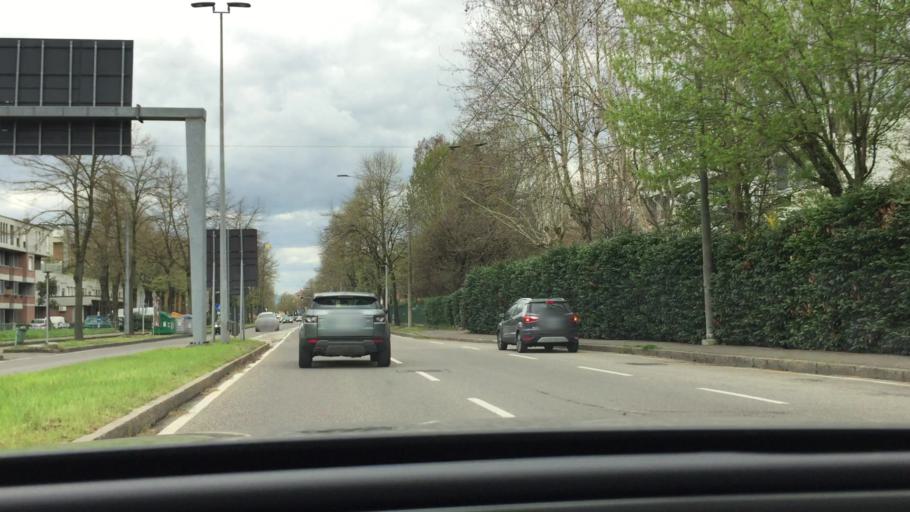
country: IT
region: Emilia-Romagna
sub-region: Provincia di Modena
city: Modena
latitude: 44.6336
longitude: 10.9020
